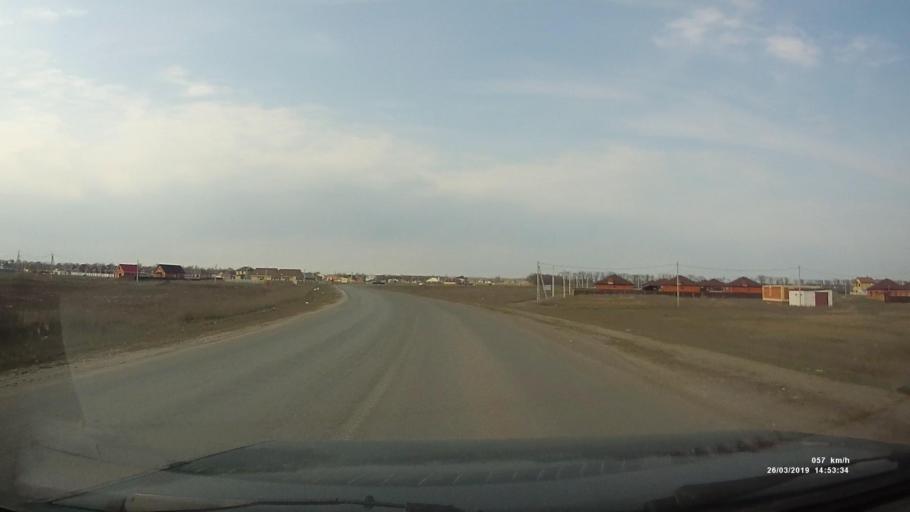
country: RU
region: Rostov
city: Novobessergenovka
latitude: 47.1859
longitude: 38.8146
